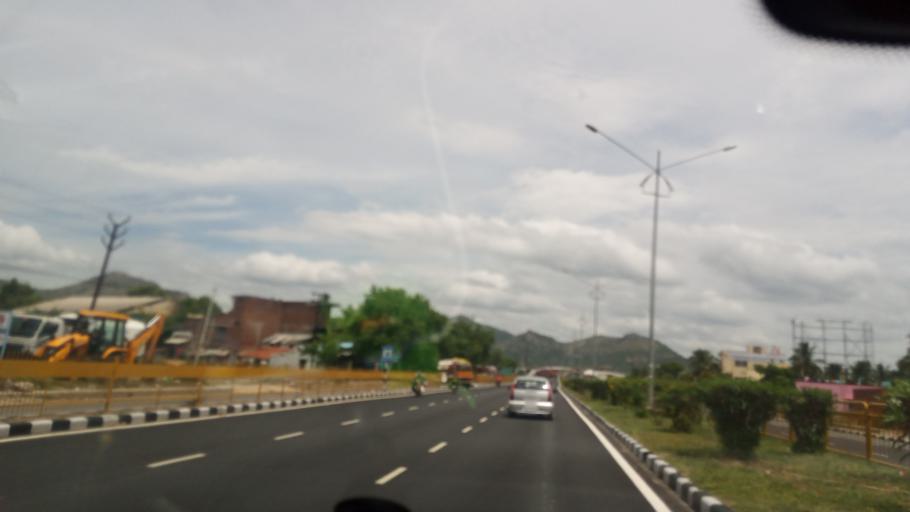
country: IN
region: Tamil Nadu
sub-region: Krishnagiri
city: Krishnagiri
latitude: 12.5202
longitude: 78.2323
